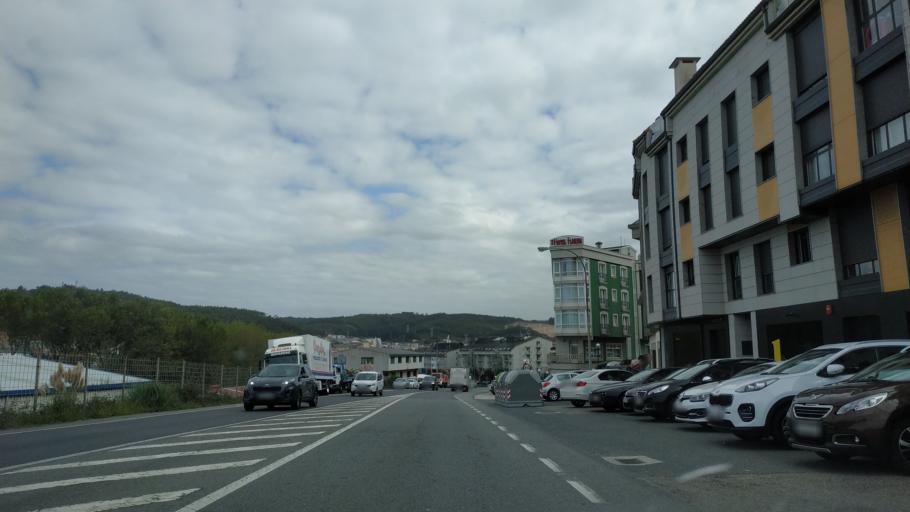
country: ES
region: Galicia
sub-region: Provincia da Coruna
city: Arteixo
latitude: 43.3160
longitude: -8.4961
